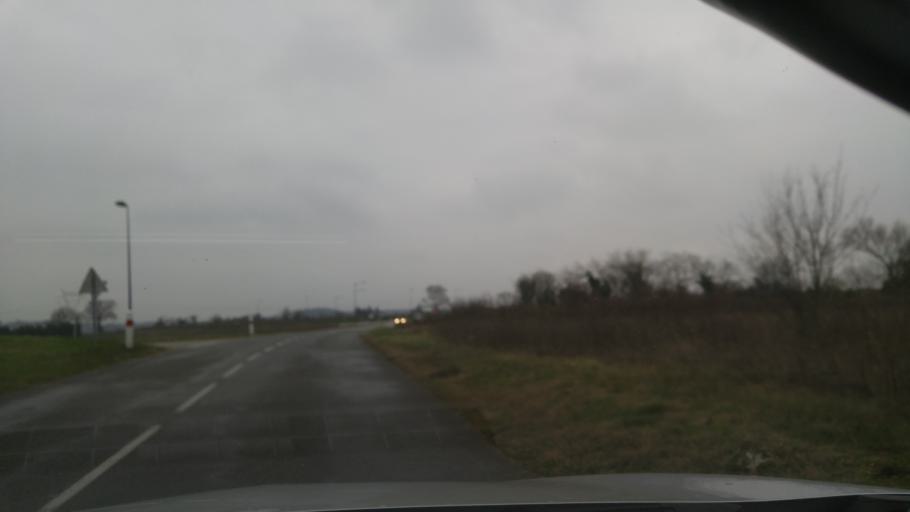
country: FR
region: Rhone-Alpes
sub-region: Departement de l'Isere
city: Charvieu-Chavagneux
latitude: 45.7235
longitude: 5.1409
